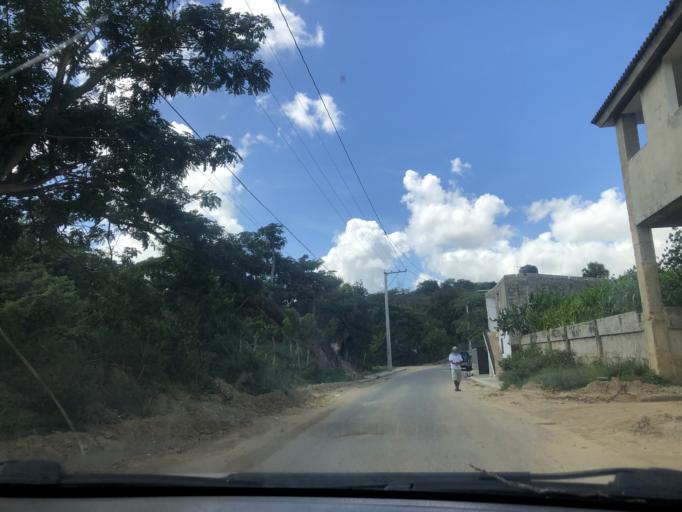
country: DO
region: Santiago
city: Santiago de los Caballeros
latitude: 19.4094
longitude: -70.7037
